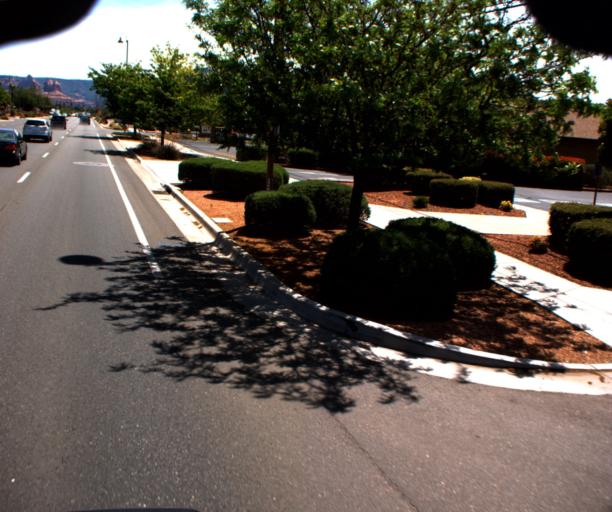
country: US
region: Arizona
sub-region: Yavapai County
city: West Sedona
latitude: 34.8624
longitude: -111.8087
